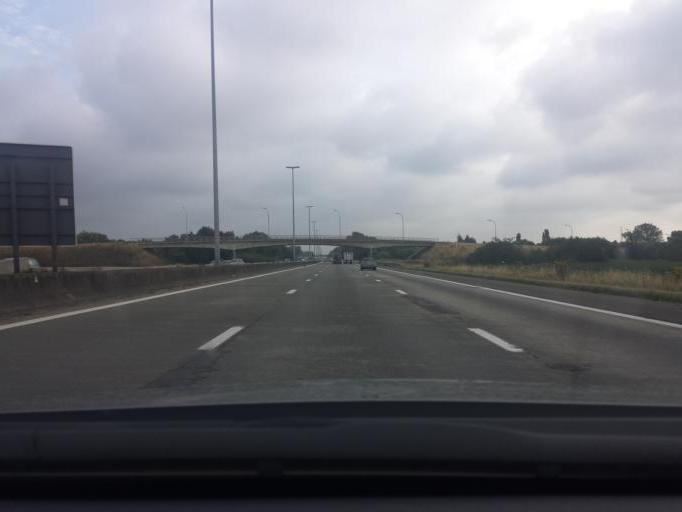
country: BE
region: Flanders
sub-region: Provincie Oost-Vlaanderen
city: Zulte
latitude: 50.8864
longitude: 3.4660
